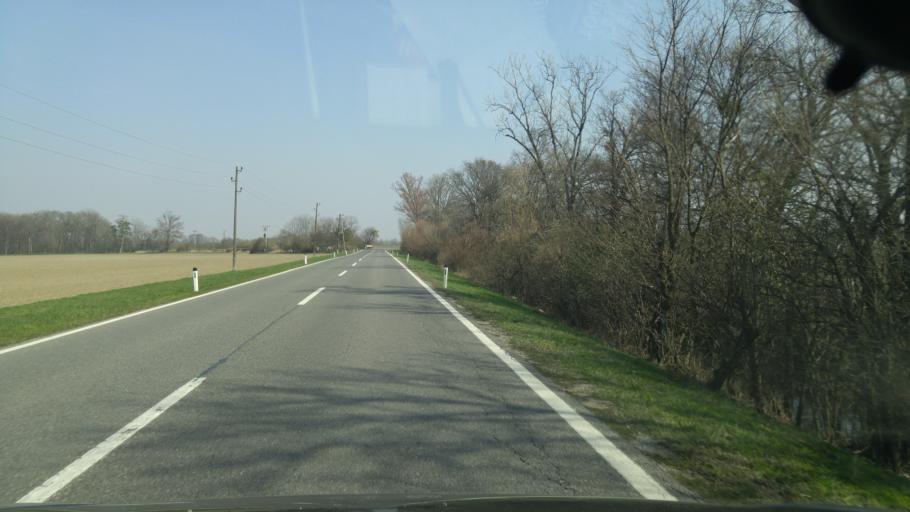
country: AT
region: Lower Austria
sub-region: Politischer Bezirk Modling
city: Laxenburg
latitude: 48.0501
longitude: 16.3617
